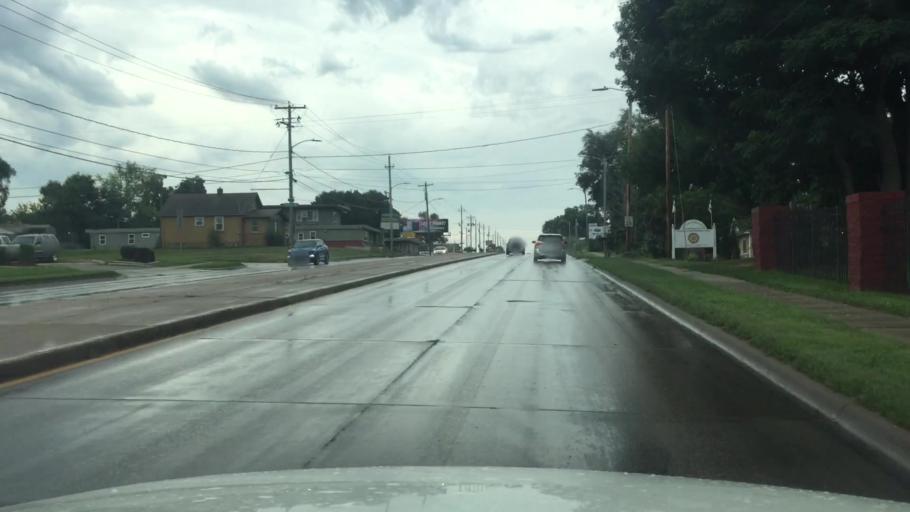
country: US
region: Iowa
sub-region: Polk County
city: Des Moines
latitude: 41.5618
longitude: -93.5970
